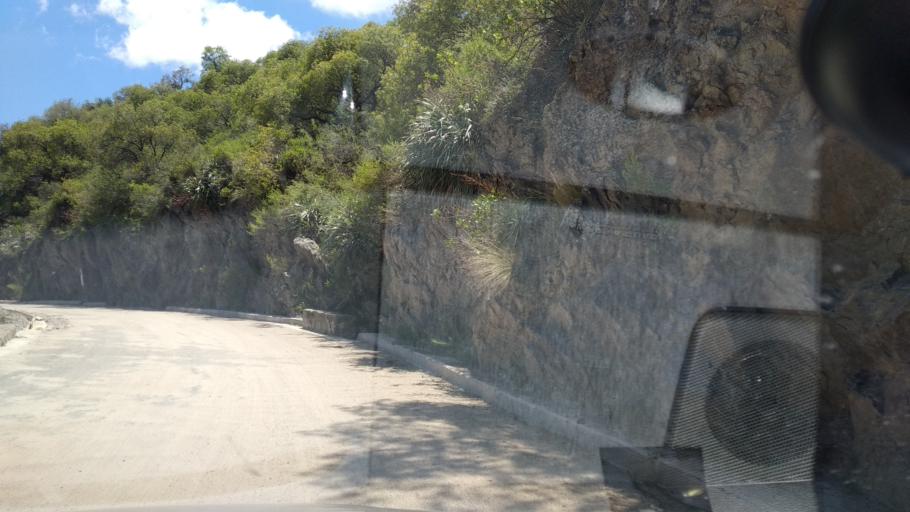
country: AR
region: Cordoba
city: Salsacate
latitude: -31.3754
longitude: -65.3902
